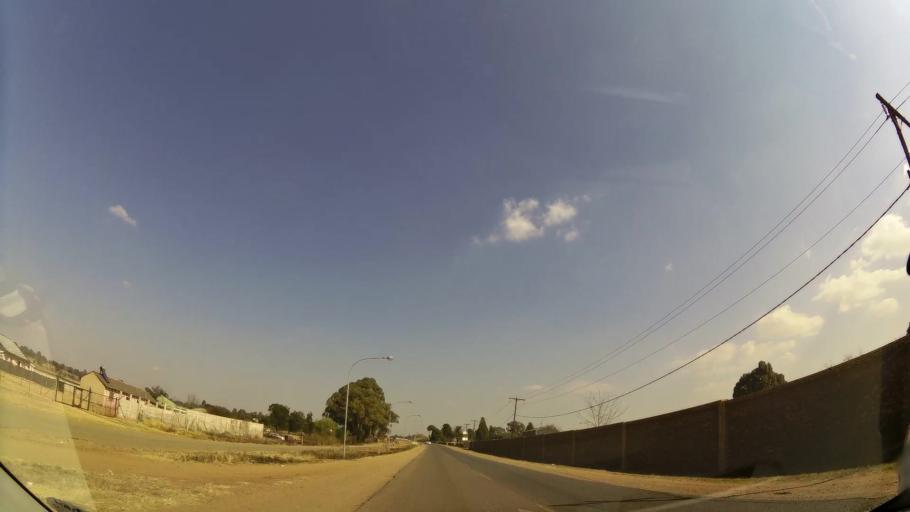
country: ZA
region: Gauteng
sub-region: Ekurhuleni Metropolitan Municipality
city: Benoni
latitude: -26.1216
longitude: 28.3980
